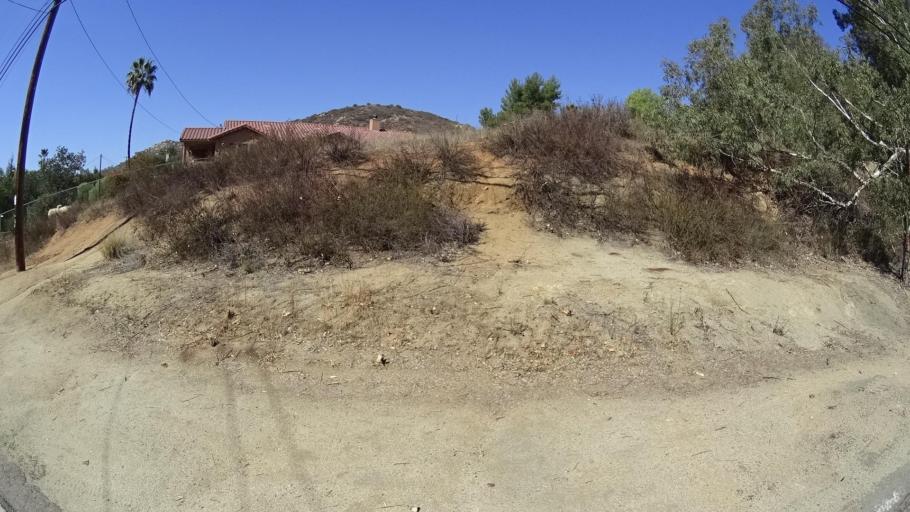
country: US
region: California
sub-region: San Diego County
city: Harbison Canyon
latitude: 32.8190
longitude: -116.8308
